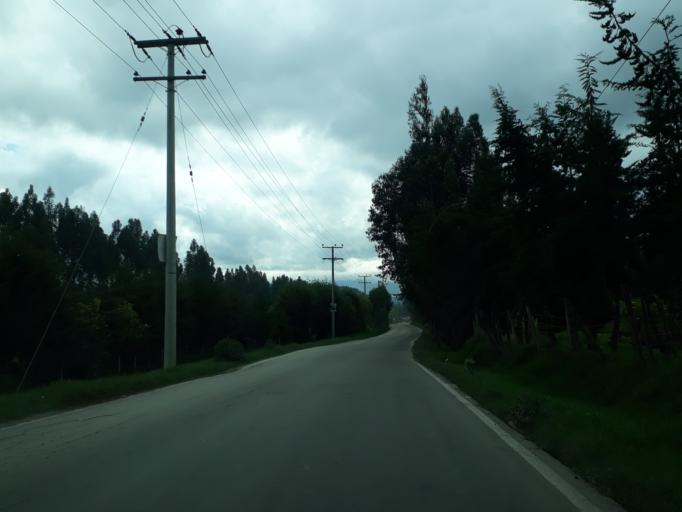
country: CO
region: Cundinamarca
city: Ubate
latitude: 5.3220
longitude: -73.7847
